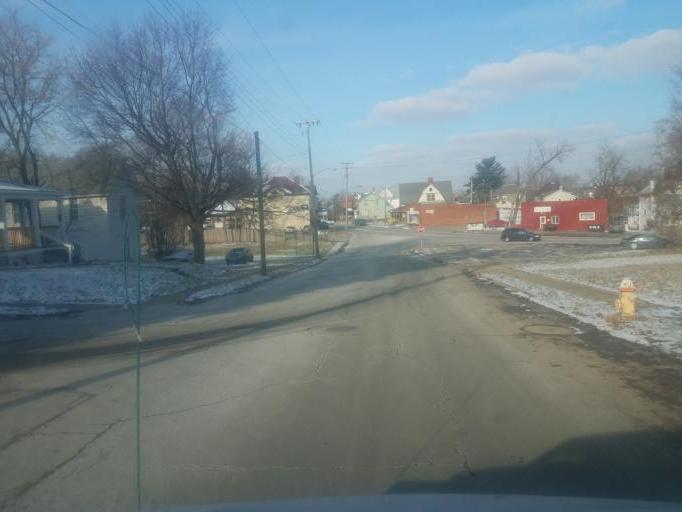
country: US
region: Ohio
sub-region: Richland County
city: Mansfield
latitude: 40.7500
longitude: -82.5133
